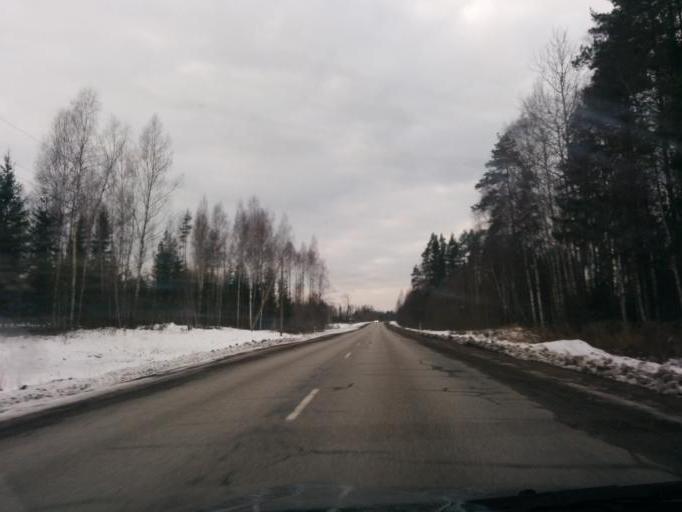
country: LV
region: Gulbenes Rajons
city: Gulbene
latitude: 57.2080
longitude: 26.6370
